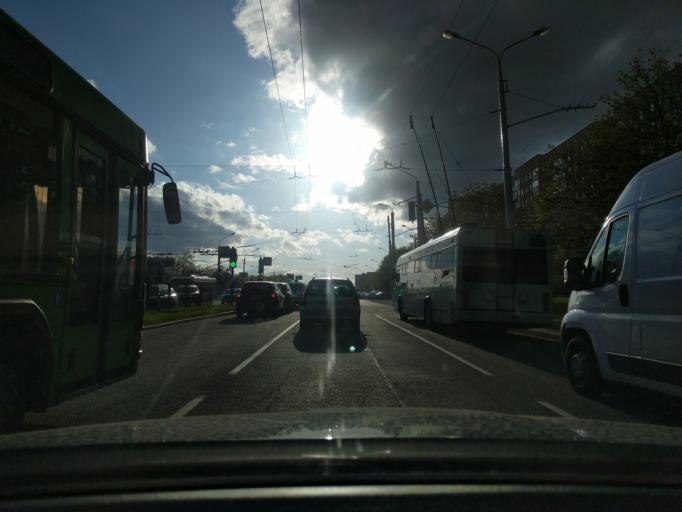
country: BY
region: Minsk
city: Novoye Medvezhino
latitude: 53.8938
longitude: 27.4855
